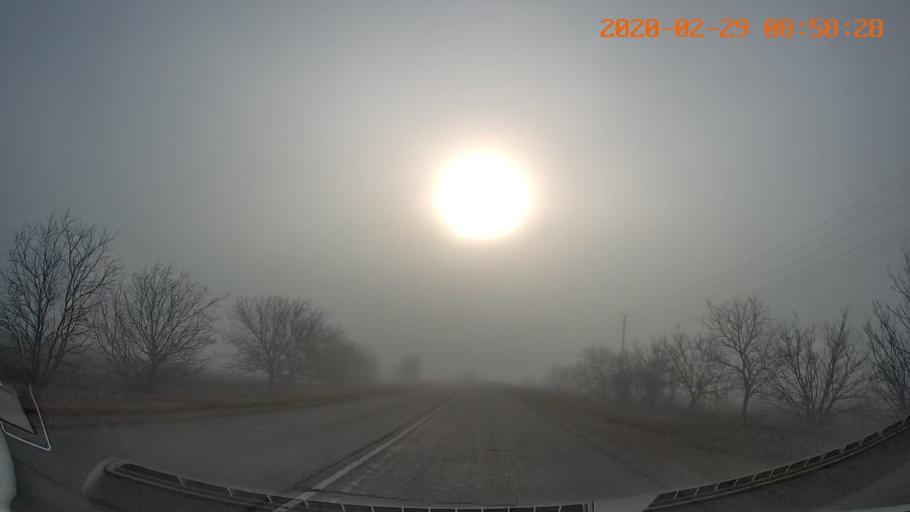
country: MD
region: Telenesti
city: Tiraspolul Nou
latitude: 46.9213
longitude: 29.6399
